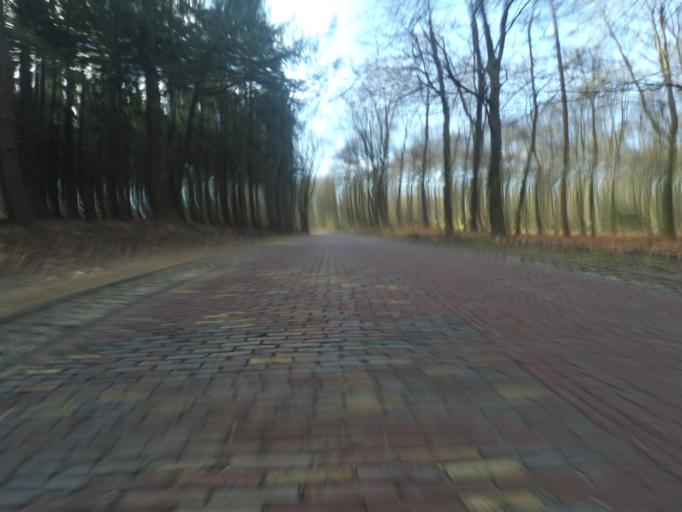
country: NL
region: Gelderland
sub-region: Gemeente Apeldoorn
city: Uddel
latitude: 52.1954
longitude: 5.8430
